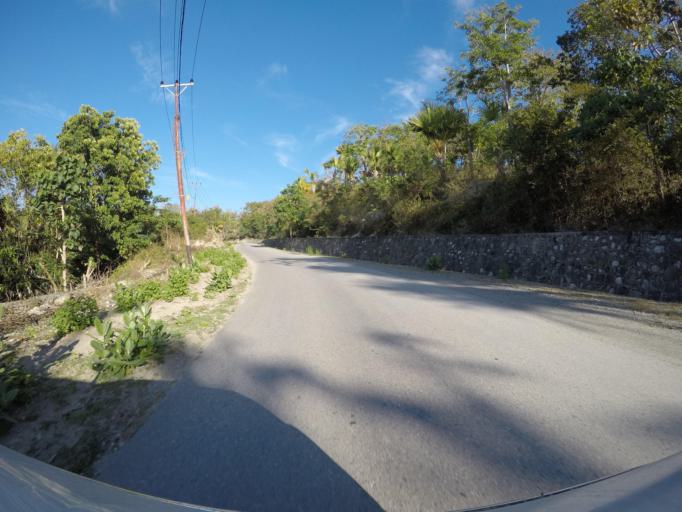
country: TL
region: Viqueque
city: Viqueque
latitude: -8.8700
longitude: 126.3506
